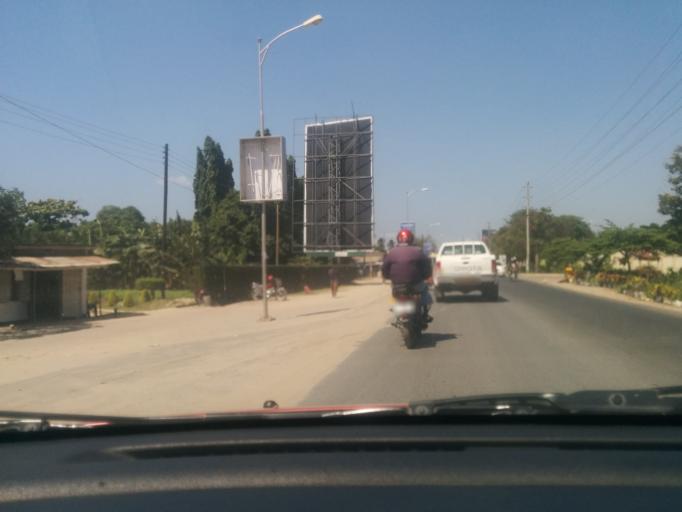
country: TZ
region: Dar es Salaam
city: Magomeni
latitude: -6.7699
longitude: 39.2190
